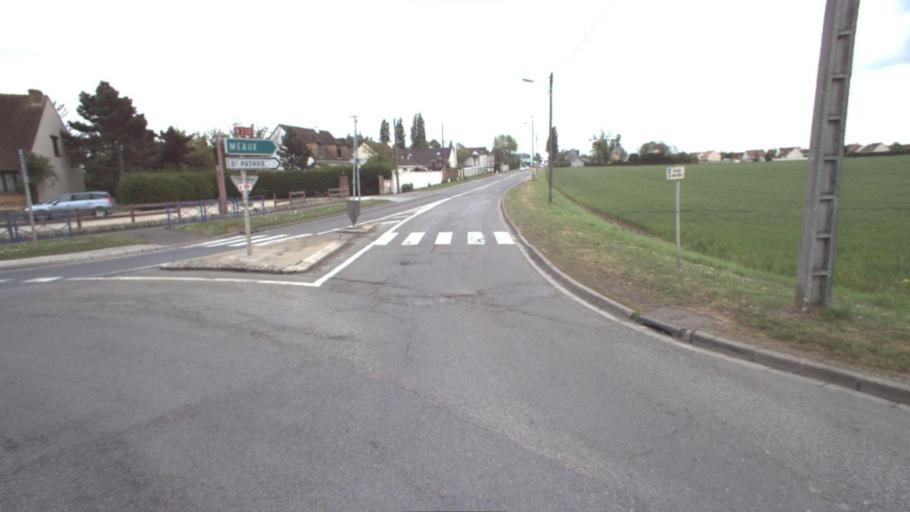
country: FR
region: Picardie
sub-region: Departement de l'Oise
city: Lagny-le-Sec
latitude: 49.0940
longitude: 2.7466
